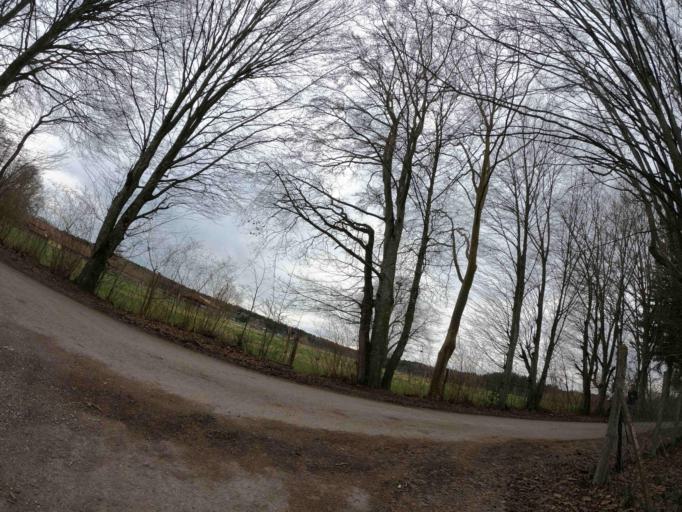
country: DE
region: Bavaria
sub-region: Upper Bavaria
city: Grunwald
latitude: 48.0173
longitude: 11.5545
